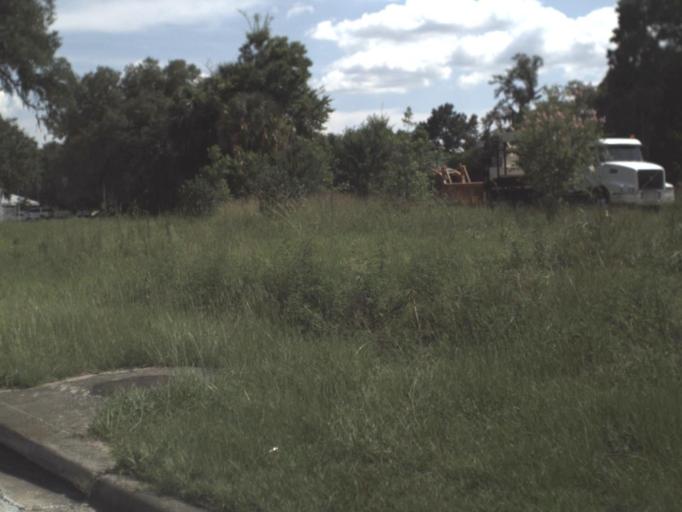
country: US
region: Florida
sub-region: Alachua County
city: Hawthorne
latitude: 29.5928
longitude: -82.0851
